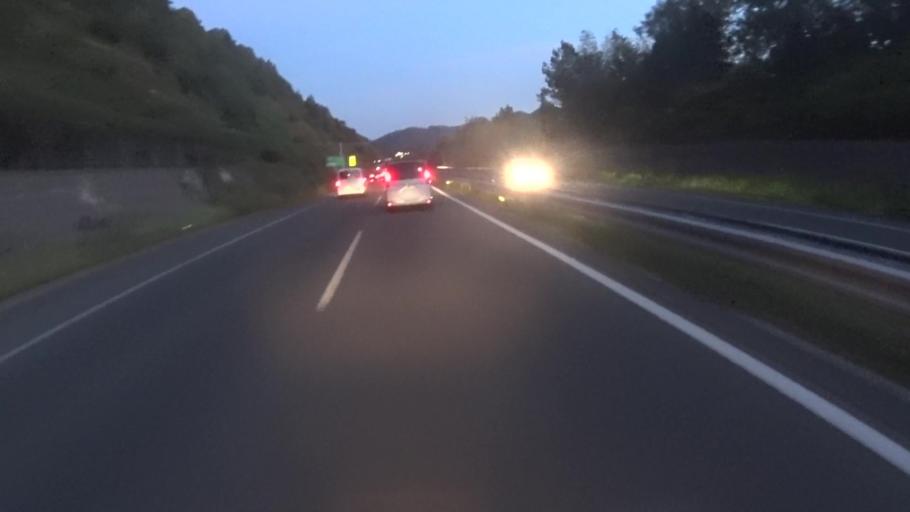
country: JP
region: Kyoto
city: Kameoka
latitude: 35.1200
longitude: 135.4804
